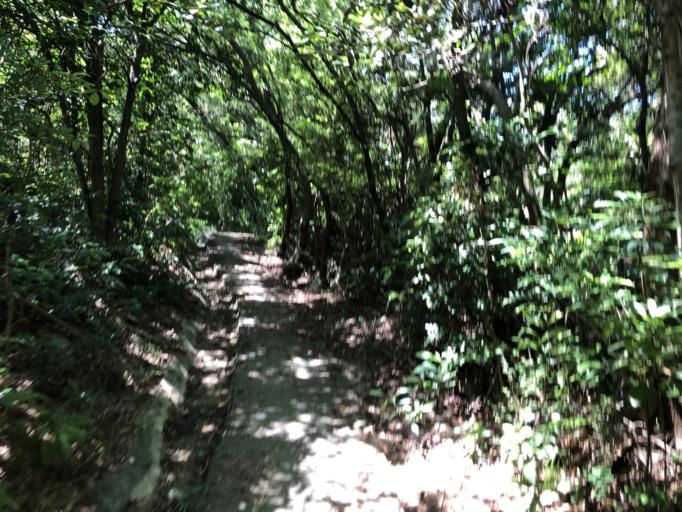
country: HK
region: Tuen Mun
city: Tuen Mun
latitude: 22.2787
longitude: 113.9884
